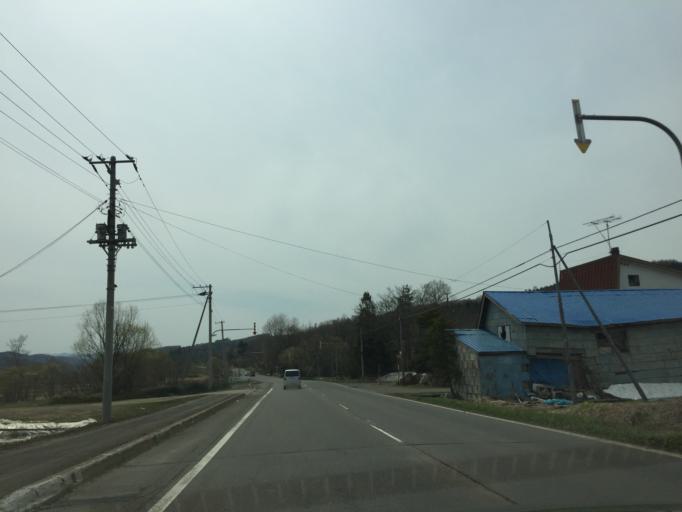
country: JP
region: Hokkaido
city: Ashibetsu
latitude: 43.5917
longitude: 142.1969
